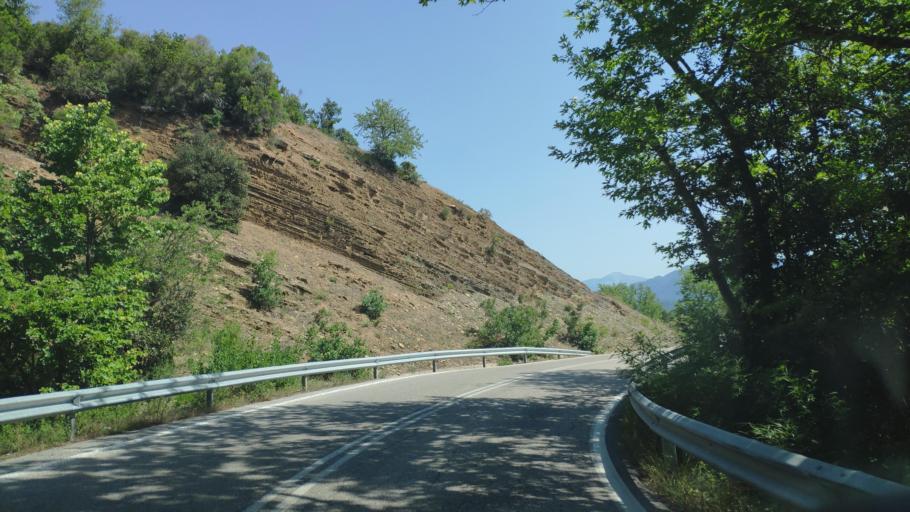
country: GR
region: West Greece
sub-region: Nomos Aitolias kai Akarnanias
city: Lepenou
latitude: 38.7994
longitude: 21.3321
